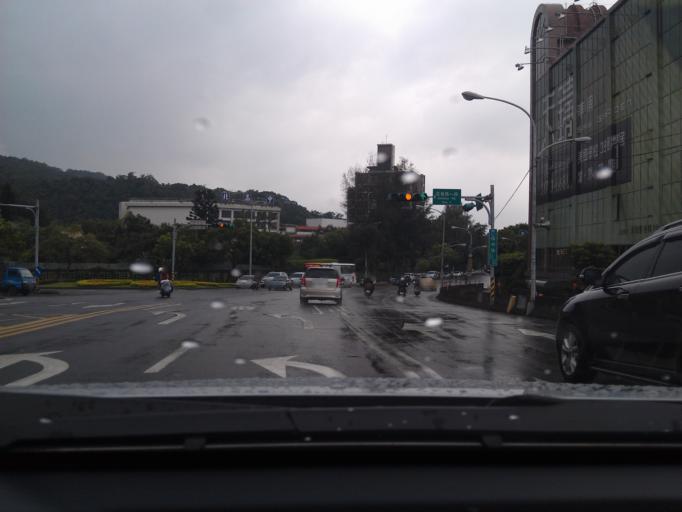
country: TW
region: Taipei
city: Taipei
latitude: 25.0998
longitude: 121.5368
